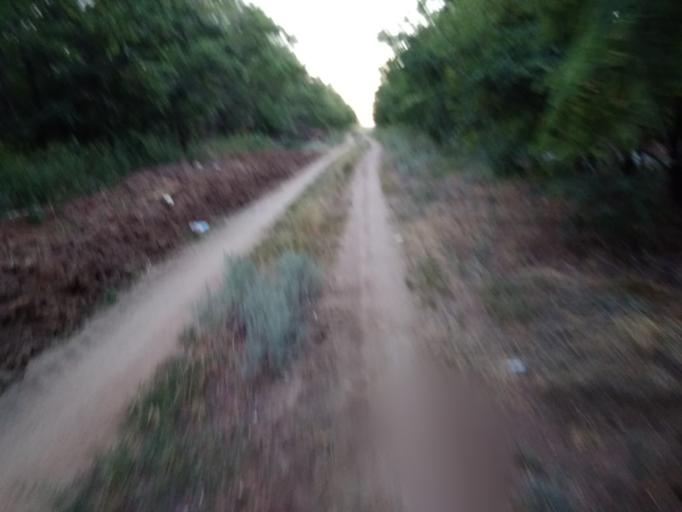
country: RU
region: Volgograd
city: Vodstroy
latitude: 48.8062
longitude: 44.5400
